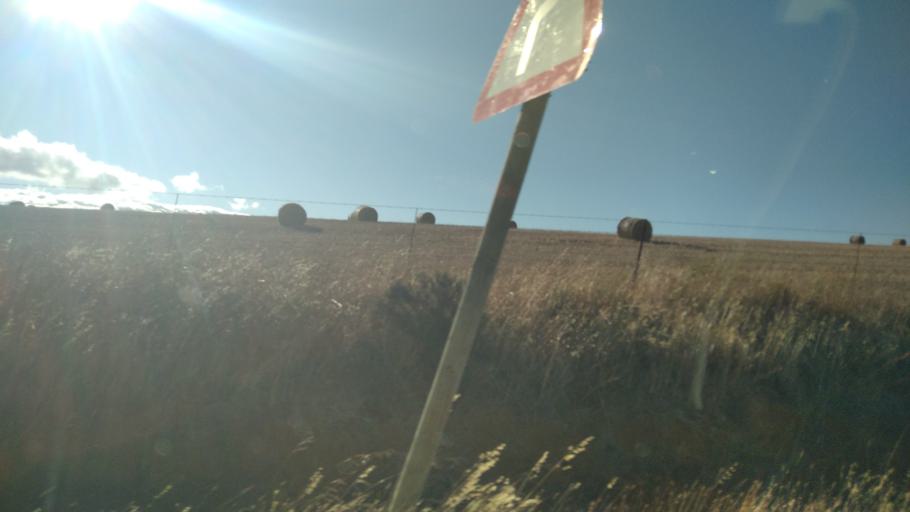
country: ZA
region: Western Cape
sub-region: Overberg District Municipality
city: Caledon
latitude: -34.1310
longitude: 19.2958
